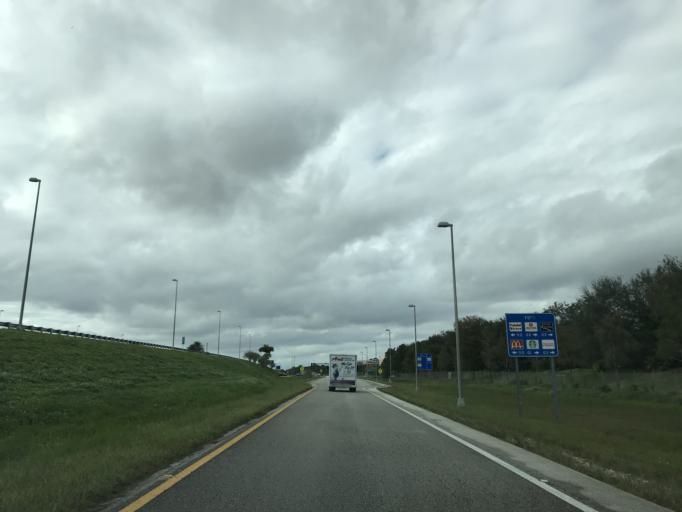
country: US
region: Florida
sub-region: Broward County
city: Coral Springs
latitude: 26.3027
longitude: -80.2756
